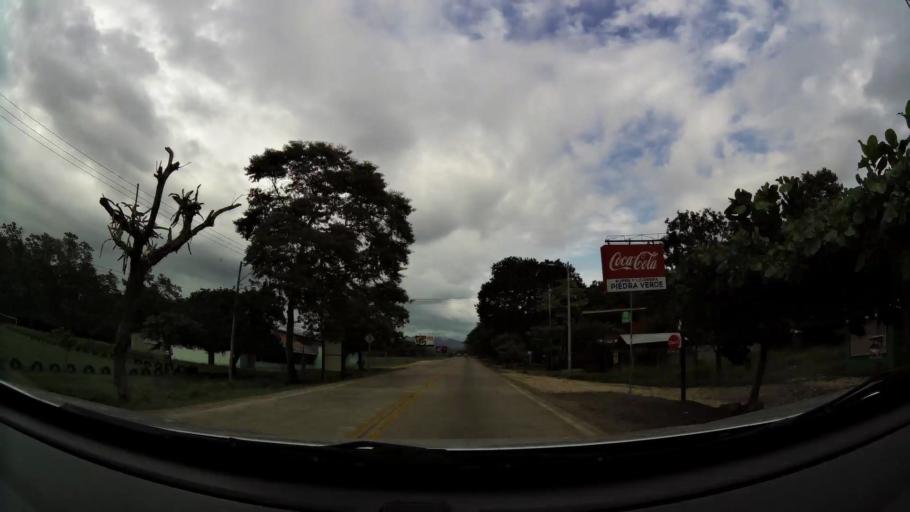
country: CR
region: Guanacaste
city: Juntas
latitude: 10.2608
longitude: -85.0387
